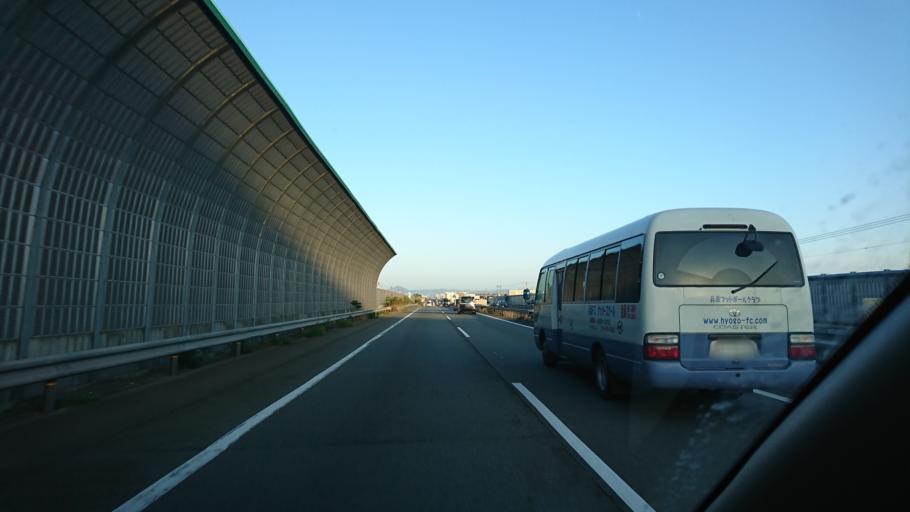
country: JP
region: Hyogo
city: Kakogawacho-honmachi
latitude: 34.7254
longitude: 134.8931
